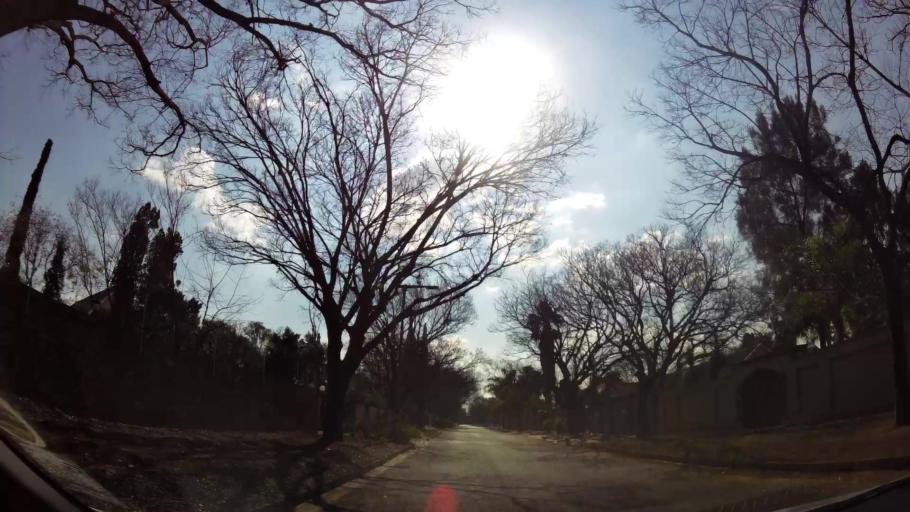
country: ZA
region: Gauteng
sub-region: Ekurhuleni Metropolitan Municipality
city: Benoni
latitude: -26.1833
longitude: 28.2876
